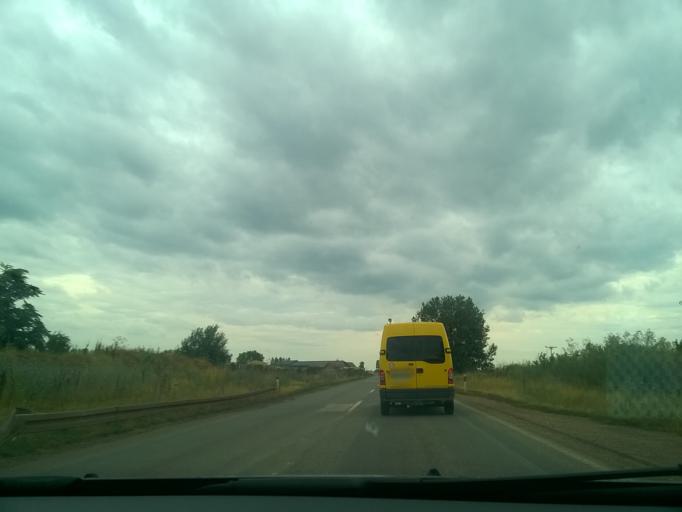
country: RS
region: Central Serbia
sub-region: Podunavski Okrug
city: Smederevo
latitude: 44.6539
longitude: 20.9684
